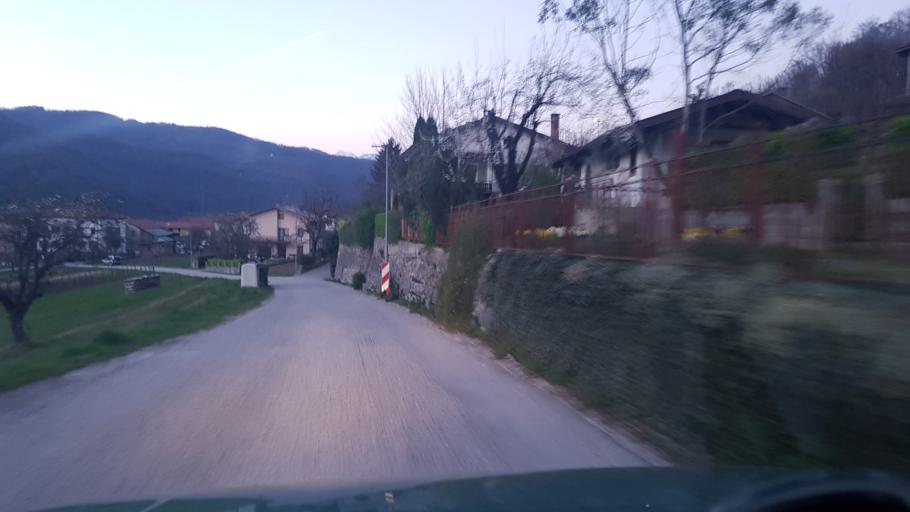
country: SI
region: Kanal
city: Kanal
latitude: 46.0737
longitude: 13.6342
